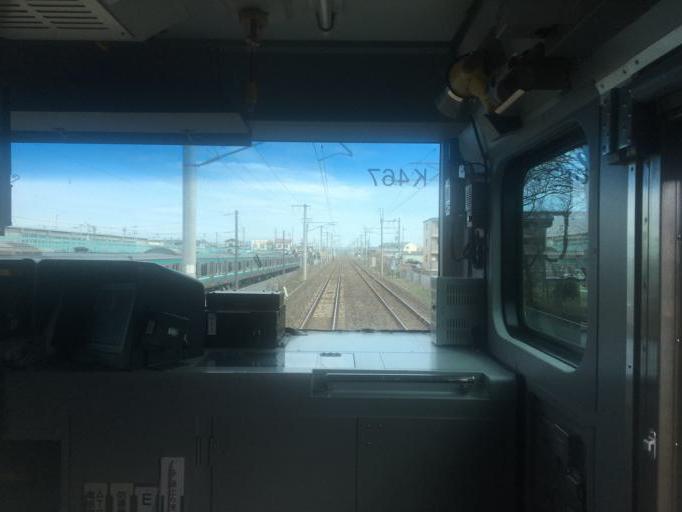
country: JP
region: Ibaraki
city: Hitachi-Naka
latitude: 36.4060
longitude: 140.5285
